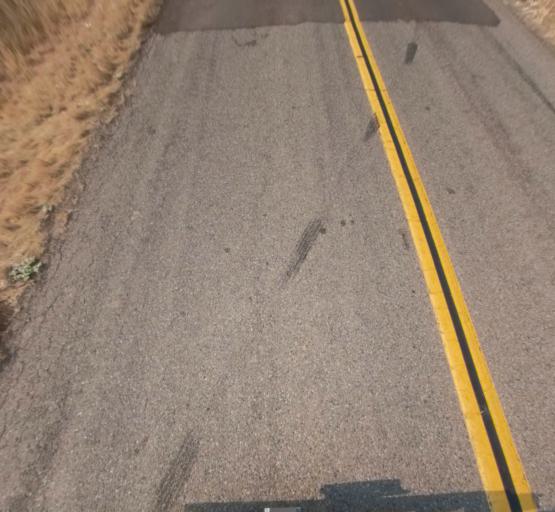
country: US
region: California
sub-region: Madera County
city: Madera Acres
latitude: 37.1249
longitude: -120.0203
